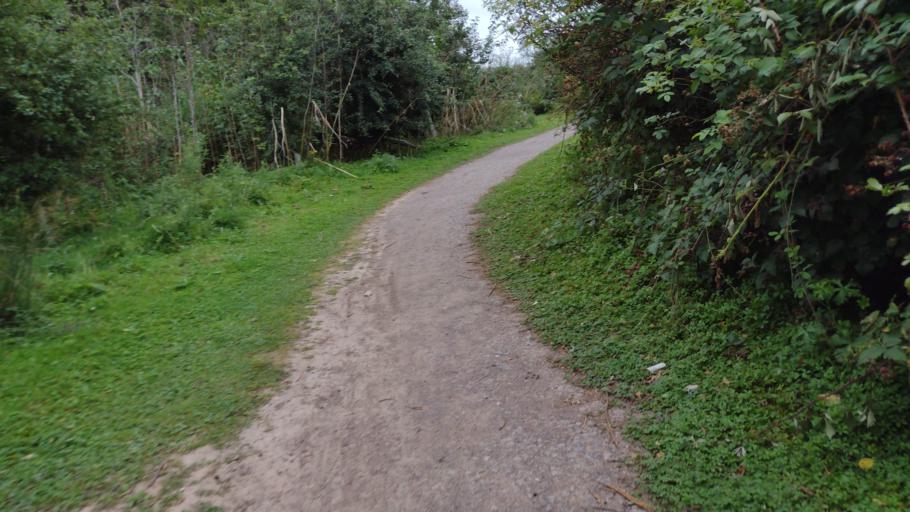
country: GB
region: England
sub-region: Wokingham
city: Winnersh
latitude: 51.4379
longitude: -0.8783
